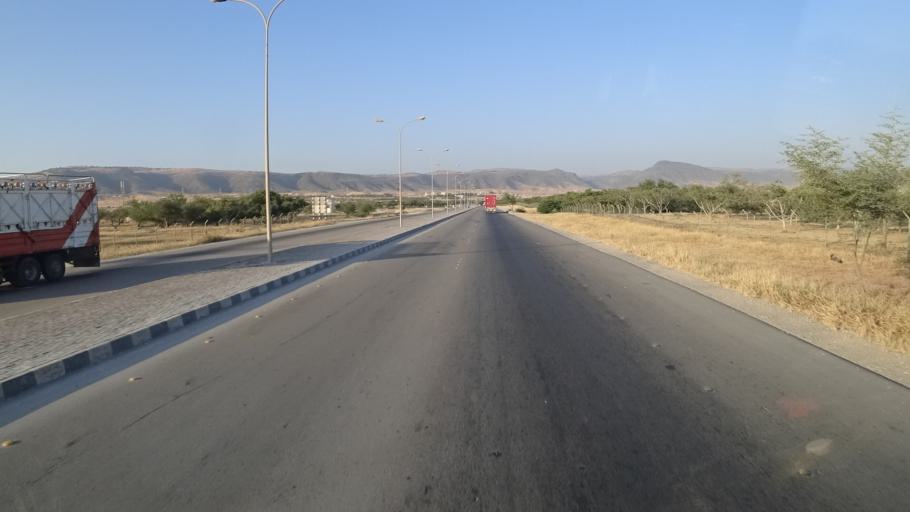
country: OM
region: Zufar
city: Salalah
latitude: 17.1063
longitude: 54.1510
